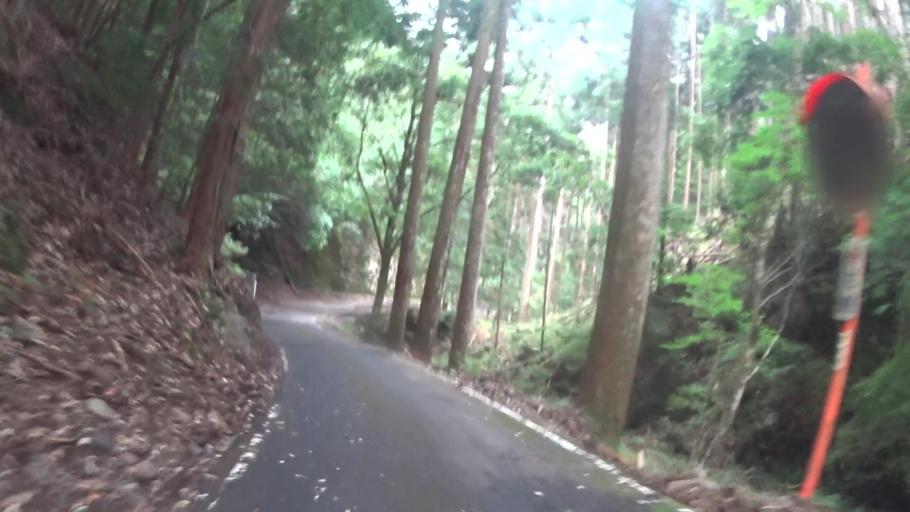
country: JP
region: Kyoto
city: Kameoka
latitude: 35.1574
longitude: 135.5728
